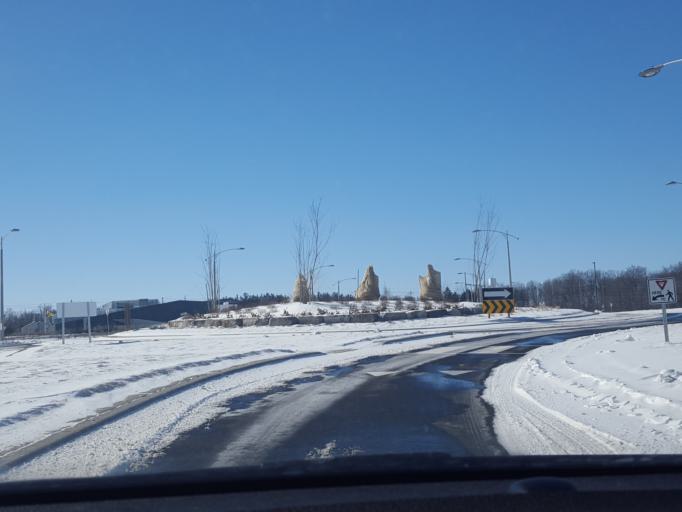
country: CA
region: Ontario
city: Waterloo
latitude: 43.4756
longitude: -80.5680
